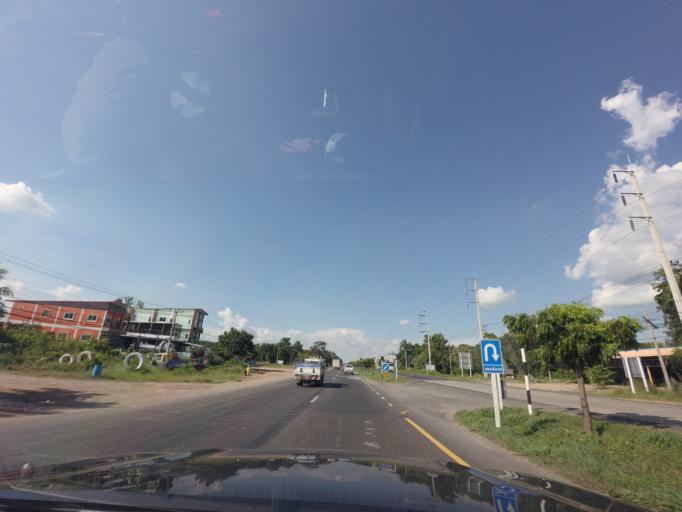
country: TH
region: Nakhon Ratchasima
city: Sida
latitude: 15.5512
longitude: 102.5489
